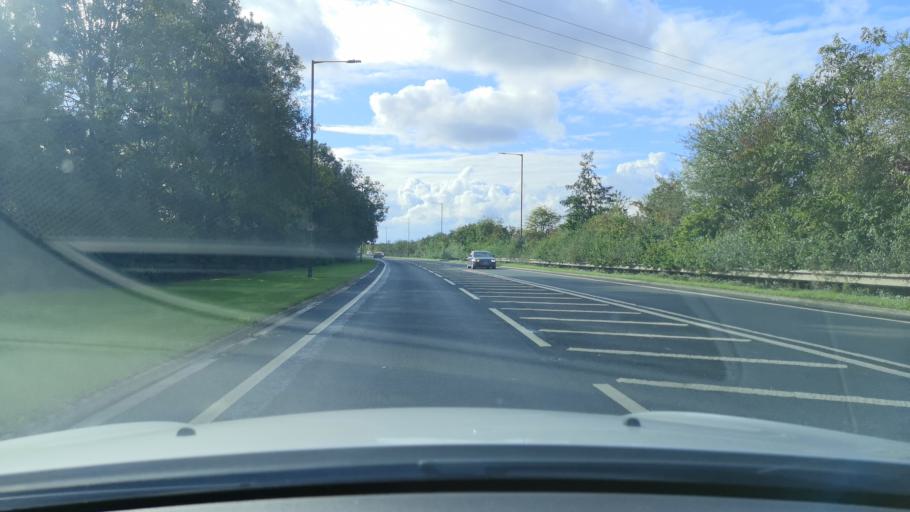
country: GB
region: England
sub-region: East Riding of Yorkshire
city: Beverley
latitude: 53.8583
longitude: -0.4396
